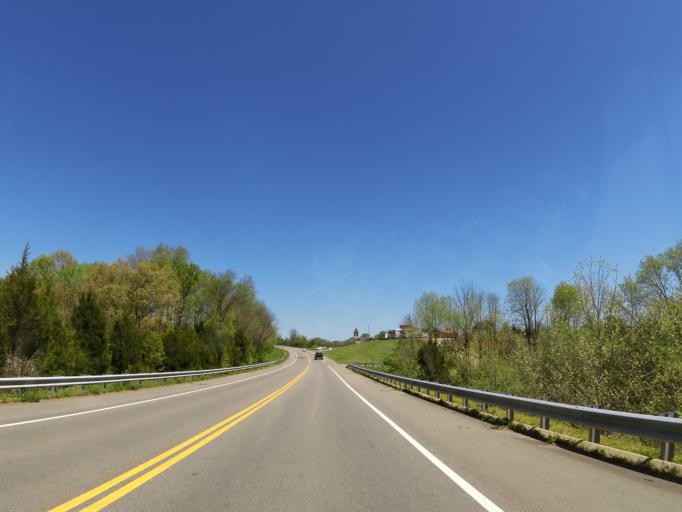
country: US
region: Tennessee
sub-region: Greene County
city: Mosheim
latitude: 36.0604
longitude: -82.9750
